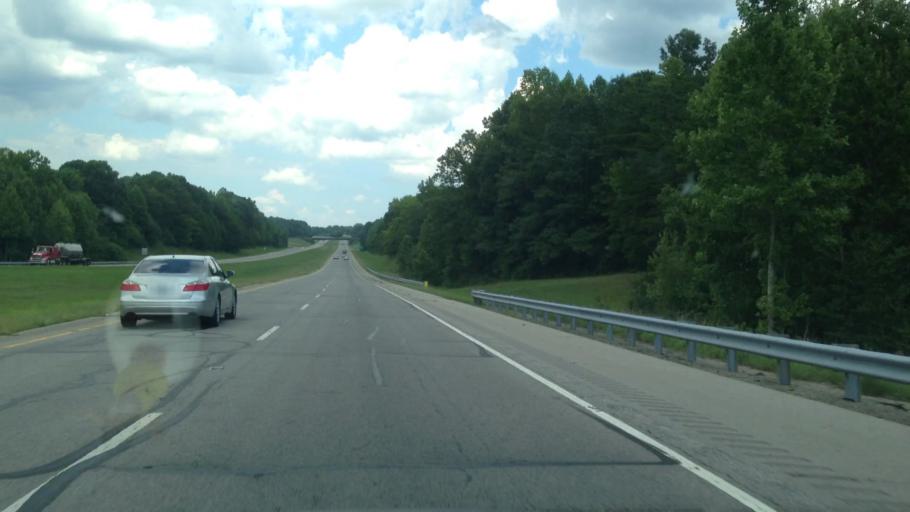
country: US
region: Virginia
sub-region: City of Danville
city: Danville
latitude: 36.4784
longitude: -79.5016
